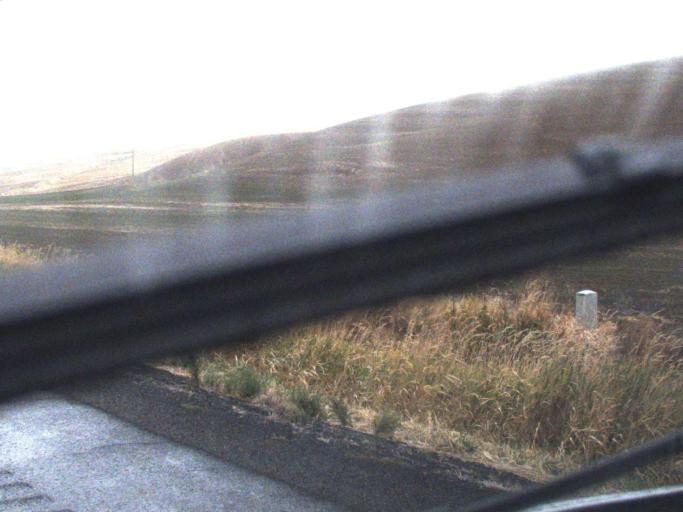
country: US
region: Washington
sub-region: Whitman County
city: Colfax
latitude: 46.8242
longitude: -117.3248
